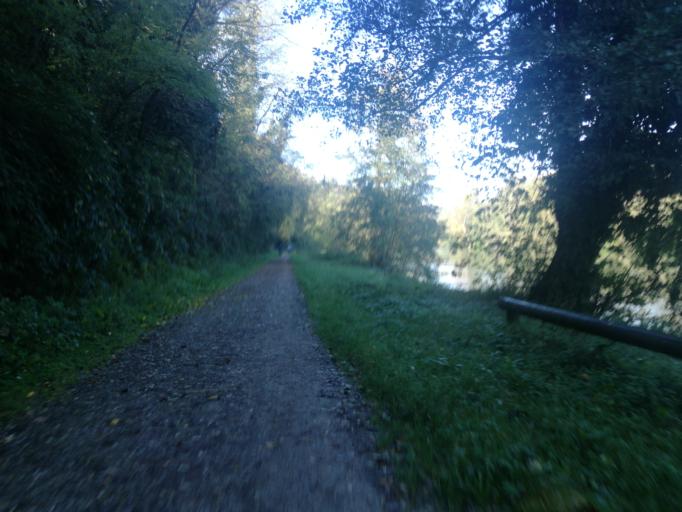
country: IT
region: Lombardy
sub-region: Provincia di Bergamo
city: Bottanuco
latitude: 45.6294
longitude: 9.4990
